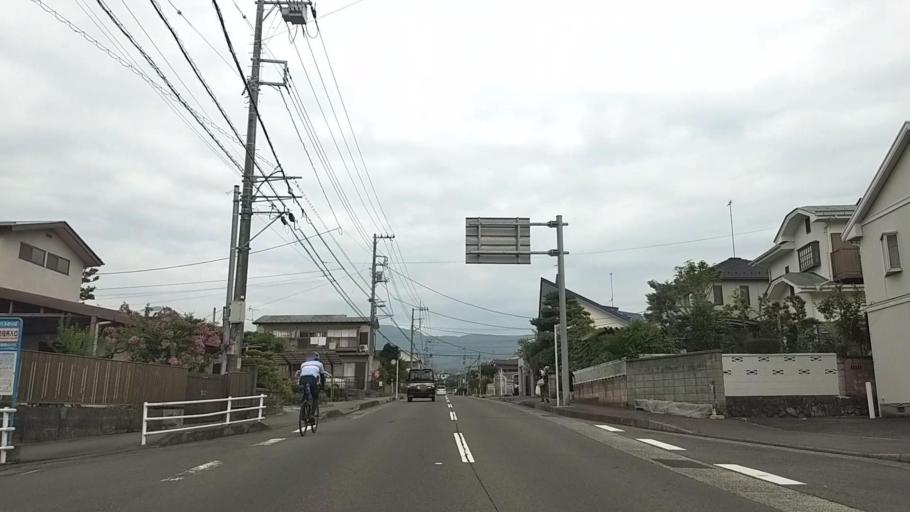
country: JP
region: Kanagawa
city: Odawara
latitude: 35.3223
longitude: 139.1021
